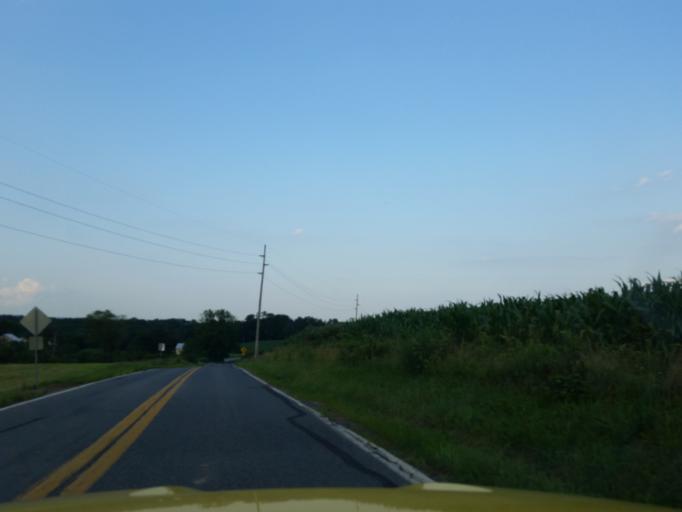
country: US
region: Pennsylvania
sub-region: Lebanon County
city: Palmyra
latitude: 40.3979
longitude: -76.6318
